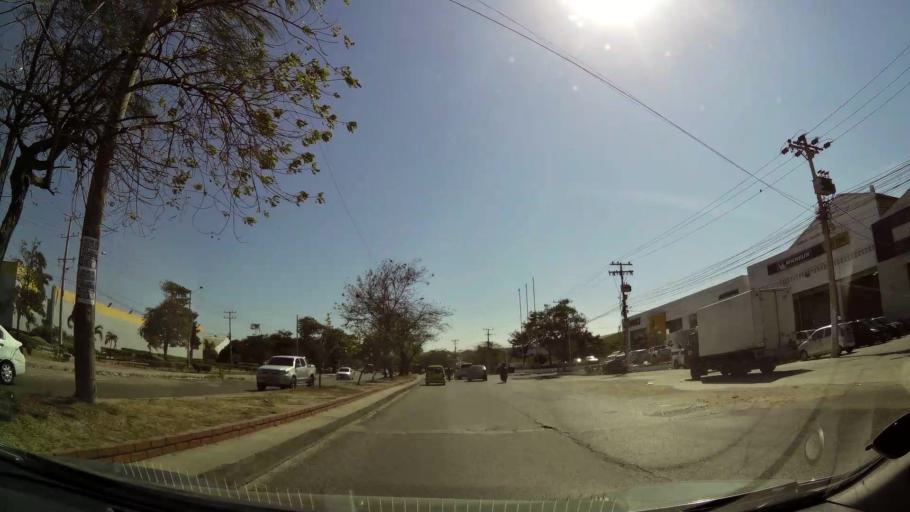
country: CO
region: Atlantico
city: Barranquilla
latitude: 10.9559
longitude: -74.7863
